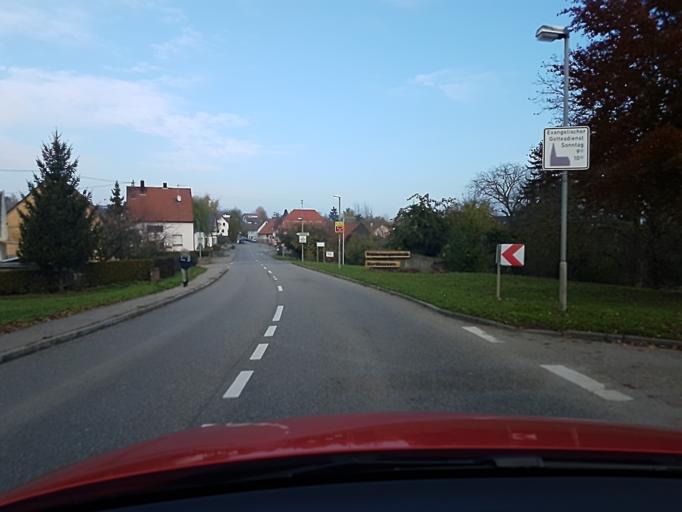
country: DE
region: Baden-Wuerttemberg
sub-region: Regierungsbezirk Stuttgart
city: Nordheim
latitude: 49.1004
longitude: 9.1042
